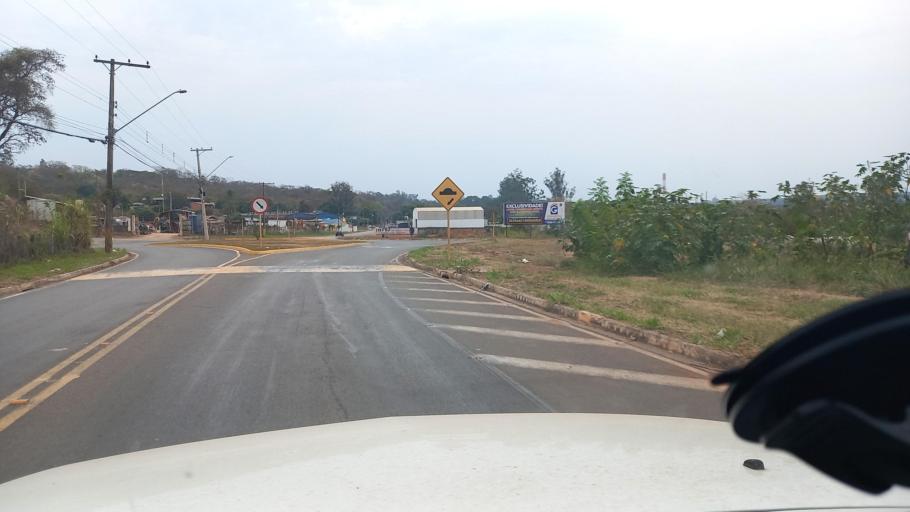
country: BR
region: Sao Paulo
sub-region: Moji-Guacu
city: Mogi-Gaucu
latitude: -22.3797
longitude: -46.9575
